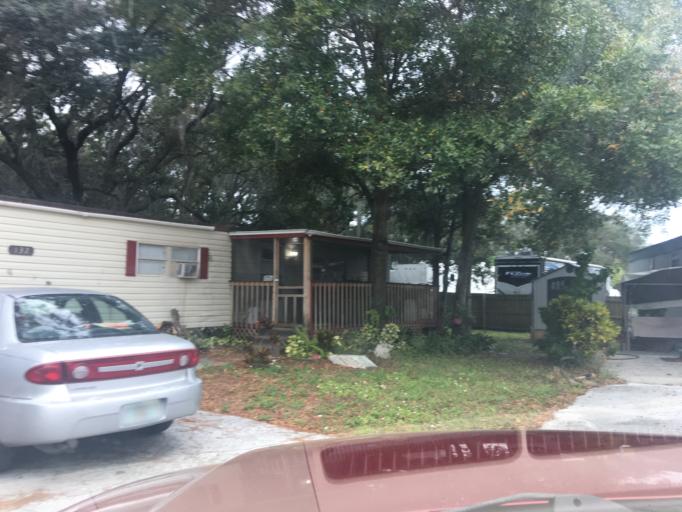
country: US
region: Florida
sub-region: Hillsborough County
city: Gibsonton
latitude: 27.8527
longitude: -82.3595
